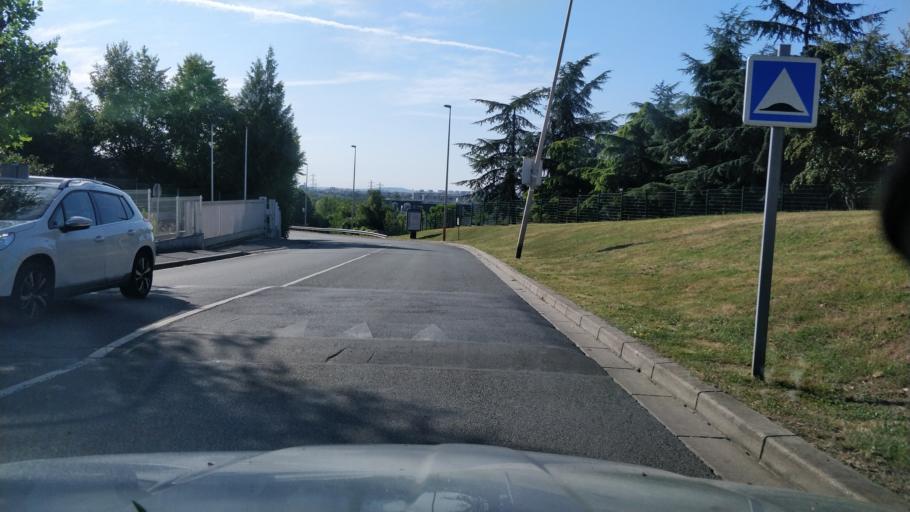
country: FR
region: Ile-de-France
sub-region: Departement de Seine-Saint-Denis
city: Villemomble
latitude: 48.8806
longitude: 2.5051
